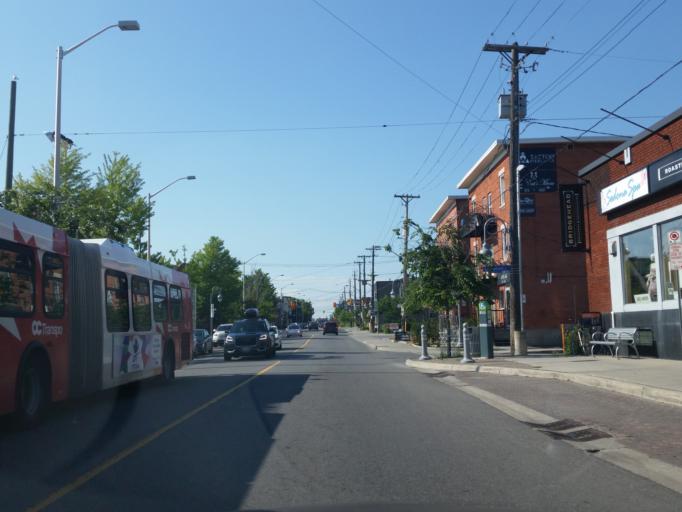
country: CA
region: Ontario
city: Ottawa
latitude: 45.4070
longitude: -75.7134
